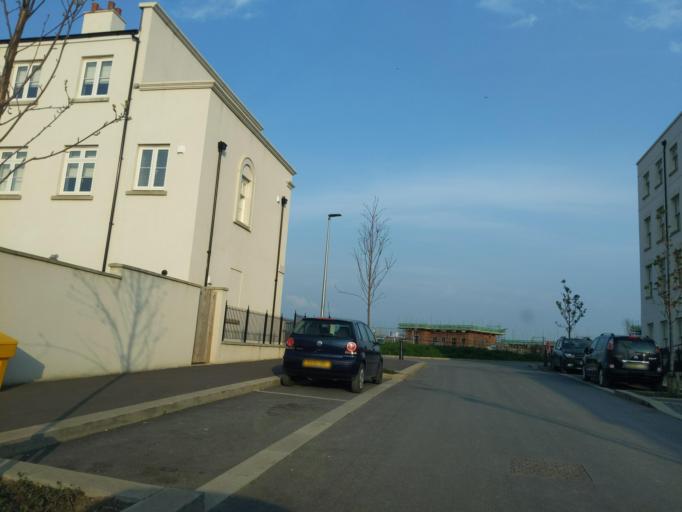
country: GB
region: England
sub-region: Devon
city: Plympton
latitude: 50.3647
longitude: -4.0484
